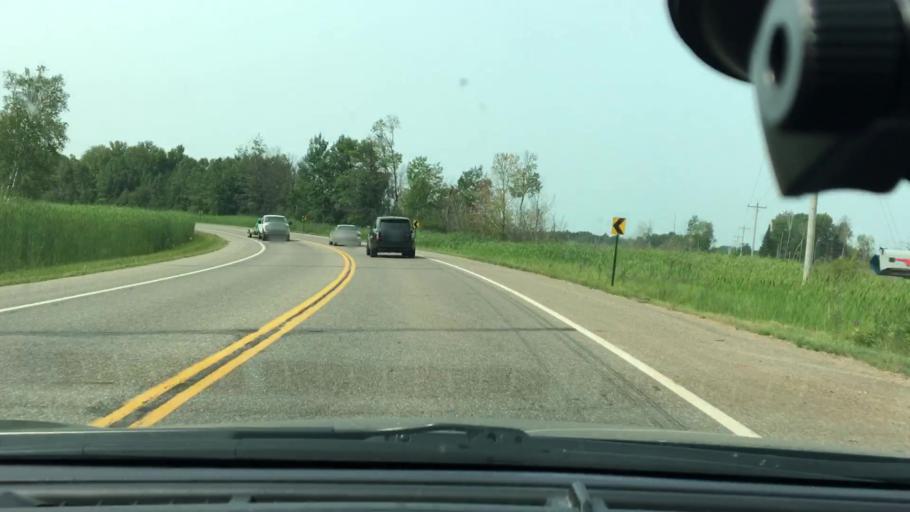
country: US
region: Minnesota
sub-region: Crow Wing County
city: Brainerd
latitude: 46.3985
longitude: -94.2211
